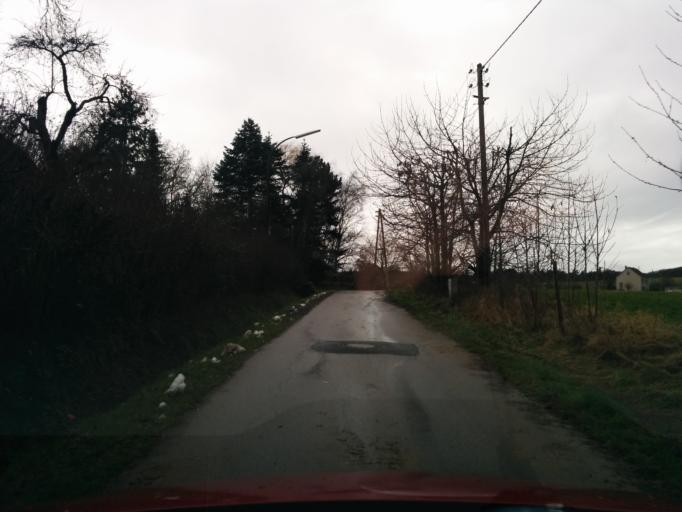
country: DE
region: North Rhine-Westphalia
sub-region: Regierungsbezirk Koln
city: Rheinbach
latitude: 50.5910
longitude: 6.9244
